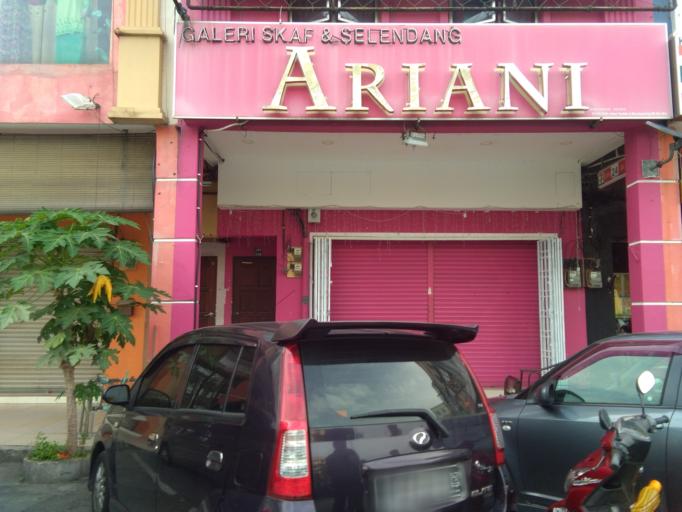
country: MY
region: Perak
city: Ipoh
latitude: 4.6013
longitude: 101.0932
